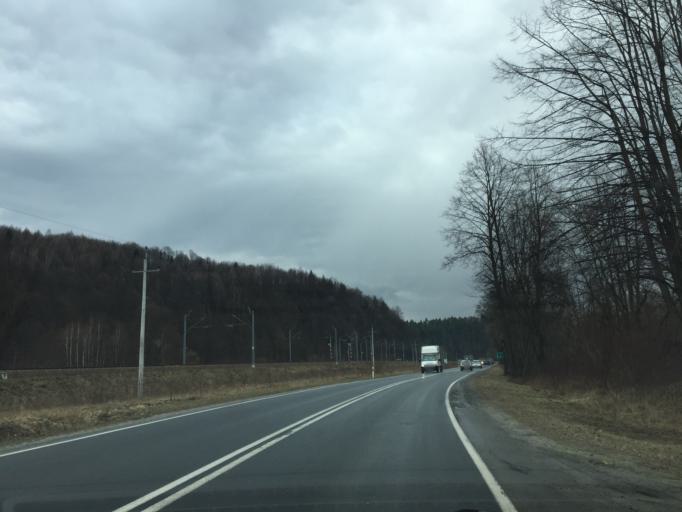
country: PL
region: Lesser Poland Voivodeship
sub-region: Powiat suski
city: Zembrzyce
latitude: 49.7629
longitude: 19.5970
